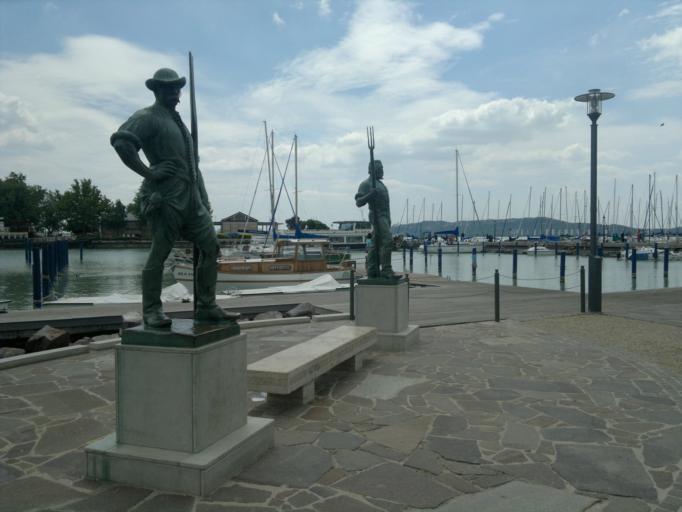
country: HU
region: Veszprem
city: Balatonfured
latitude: 46.9534
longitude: 17.8945
